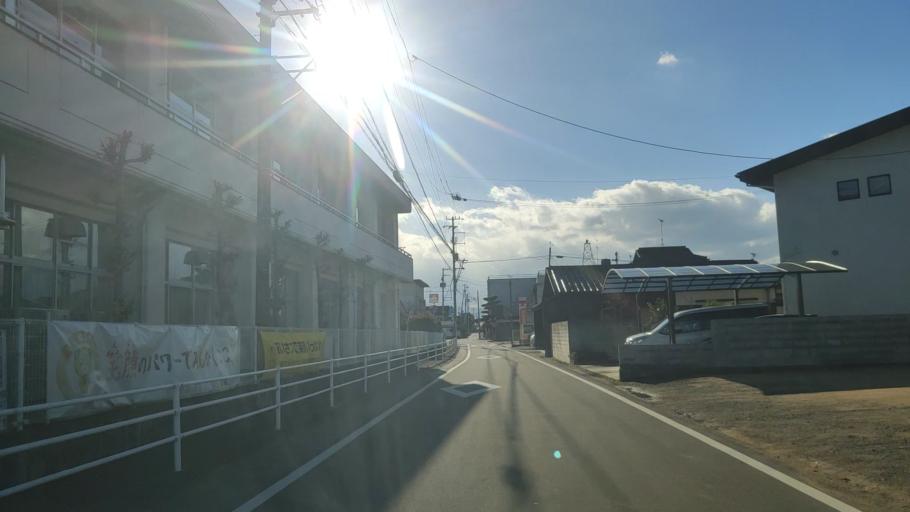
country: JP
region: Ehime
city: Saijo
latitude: 33.9136
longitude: 133.1007
